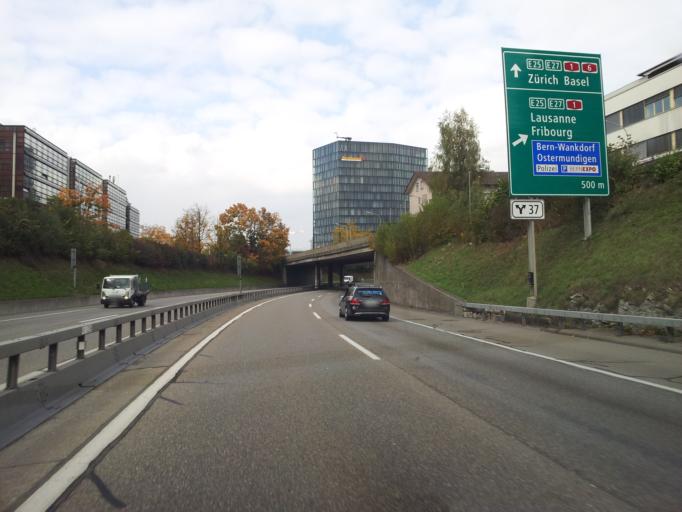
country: CH
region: Bern
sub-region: Bern-Mittelland District
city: Bern
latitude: 46.9546
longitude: 7.4692
